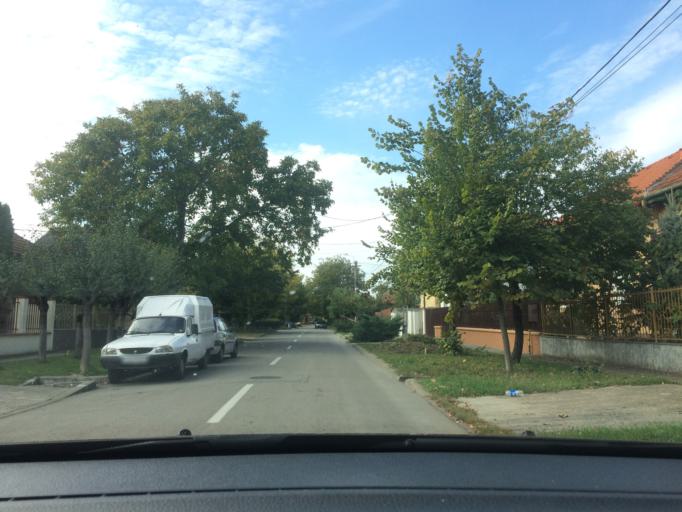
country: RO
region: Timis
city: Timisoara
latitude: 45.7576
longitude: 21.2007
